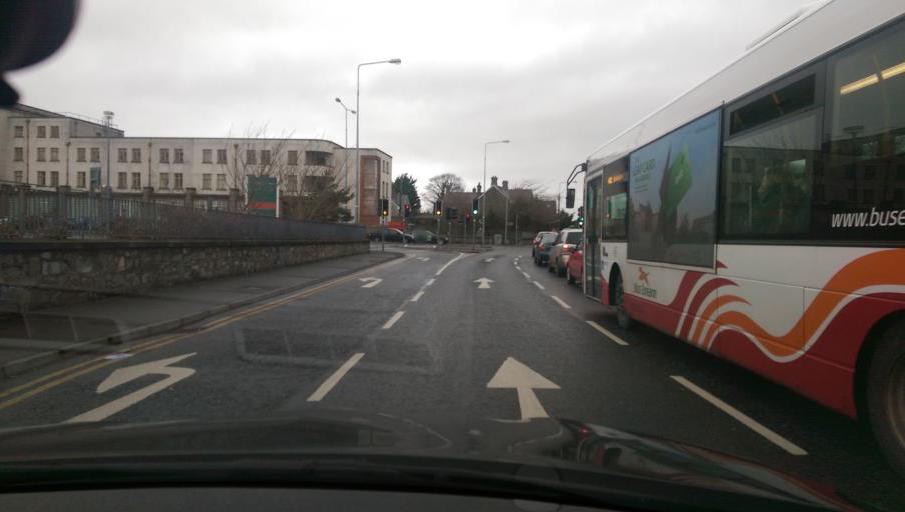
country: IE
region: Connaught
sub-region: County Galway
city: Gaillimh
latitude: 53.2765
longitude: -9.0636
